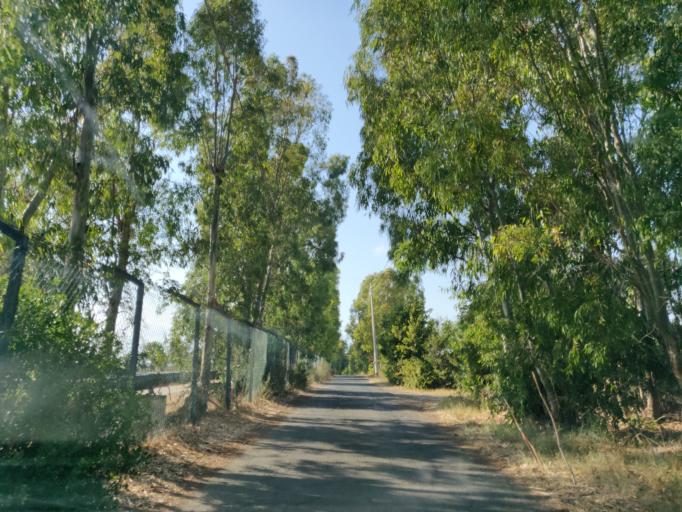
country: IT
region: Latium
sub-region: Citta metropolitana di Roma Capitale
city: Aurelia
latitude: 42.1350
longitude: 11.7620
